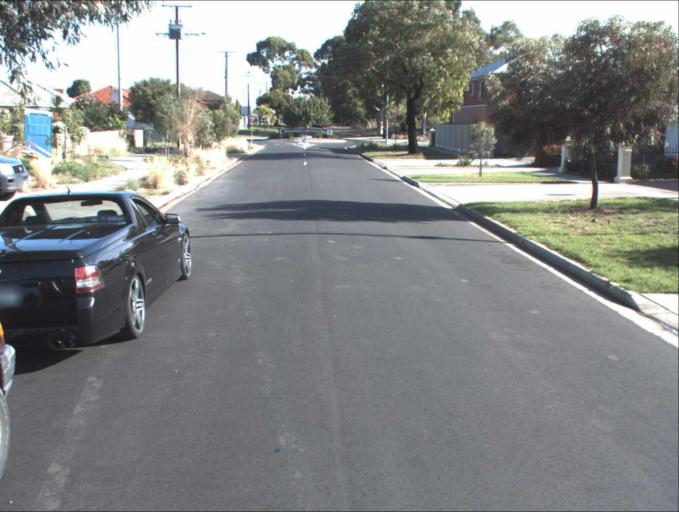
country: AU
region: South Australia
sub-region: Charles Sturt
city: Woodville North
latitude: -34.8613
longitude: 138.5520
